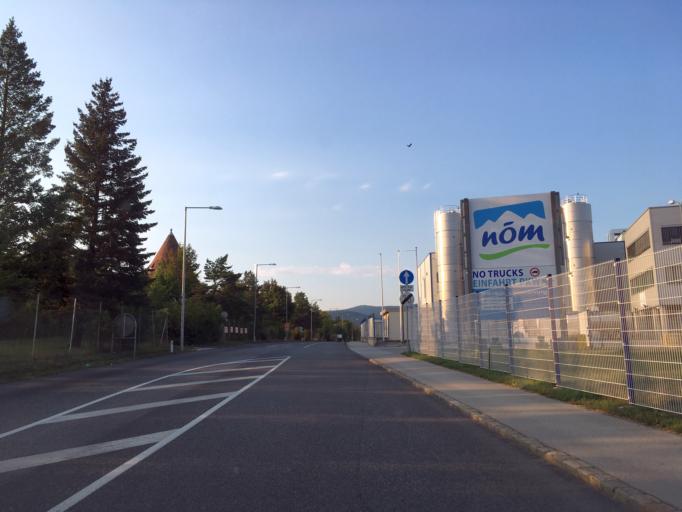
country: AT
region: Lower Austria
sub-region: Politischer Bezirk Baden
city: Baden
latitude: 47.9911
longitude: 16.2252
